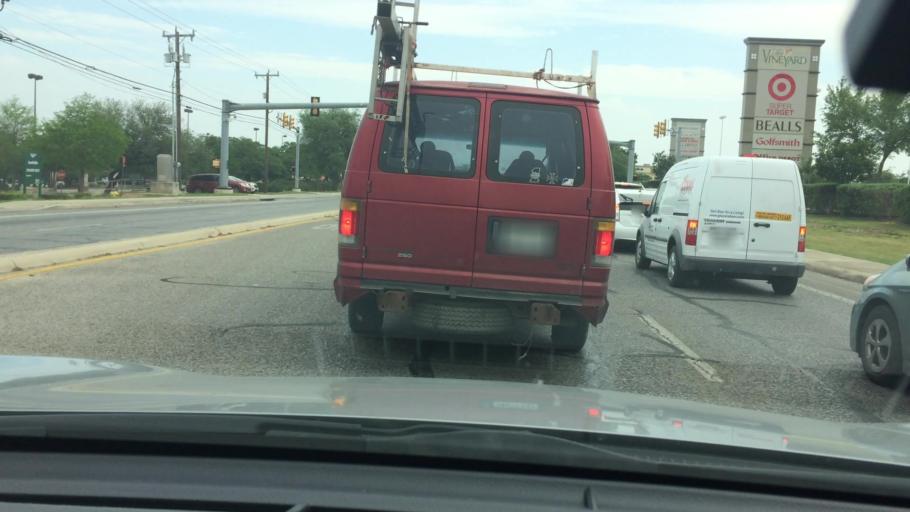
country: US
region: Texas
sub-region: Bexar County
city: Hollywood Park
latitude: 29.6127
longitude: -98.5090
